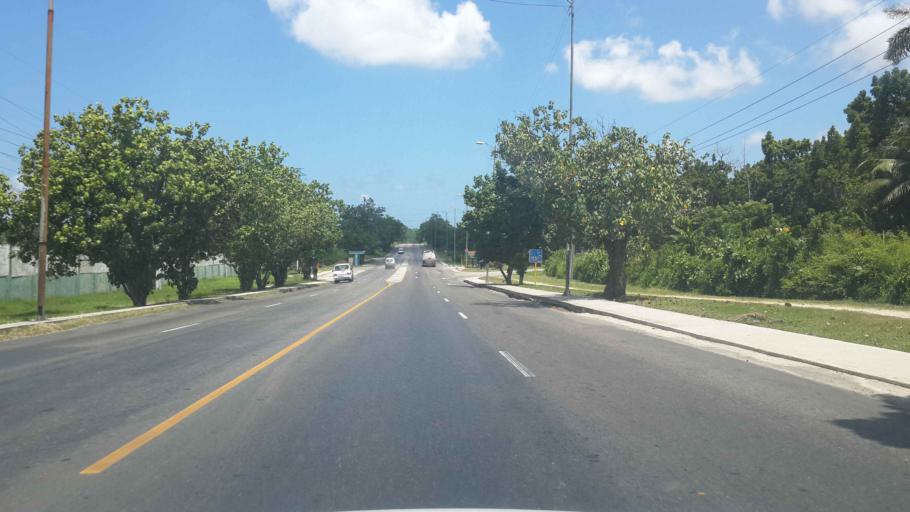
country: CU
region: La Habana
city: Guanabacoa
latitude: 23.1359
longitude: -82.3087
